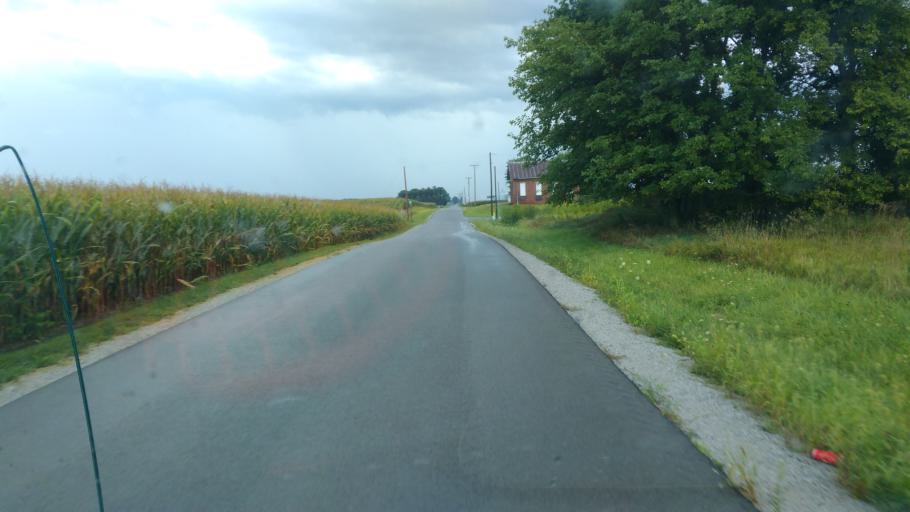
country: US
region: Ohio
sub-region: Hardin County
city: Kenton
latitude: 40.6894
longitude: -83.6351
